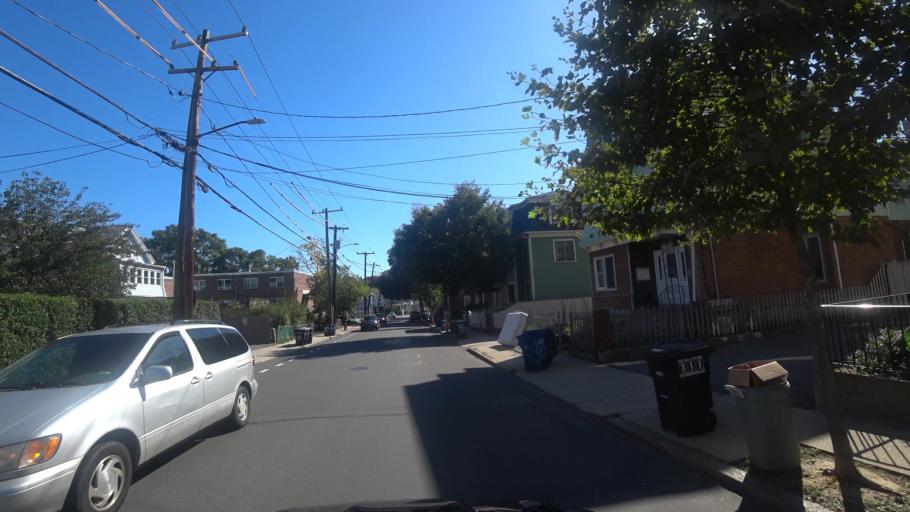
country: US
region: Massachusetts
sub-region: Middlesex County
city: Somerville
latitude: 42.3849
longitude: -71.1017
